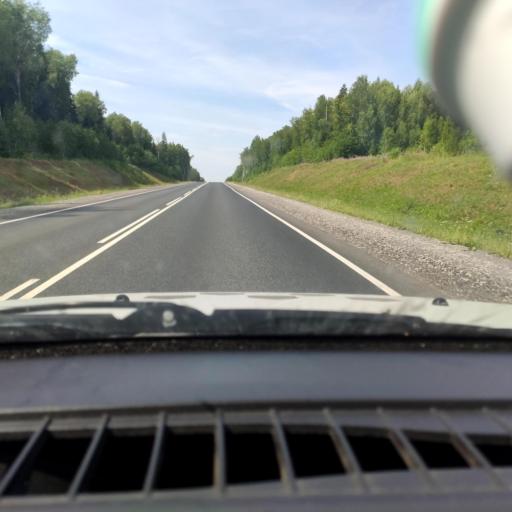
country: RU
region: Kirov
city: Kostino
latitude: 58.6630
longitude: 53.7635
